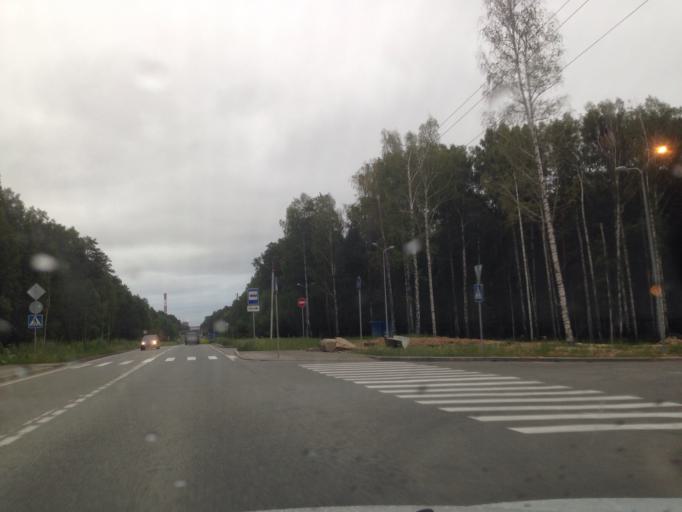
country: RU
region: Sverdlovsk
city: Istok
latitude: 56.8394
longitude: 60.7895
